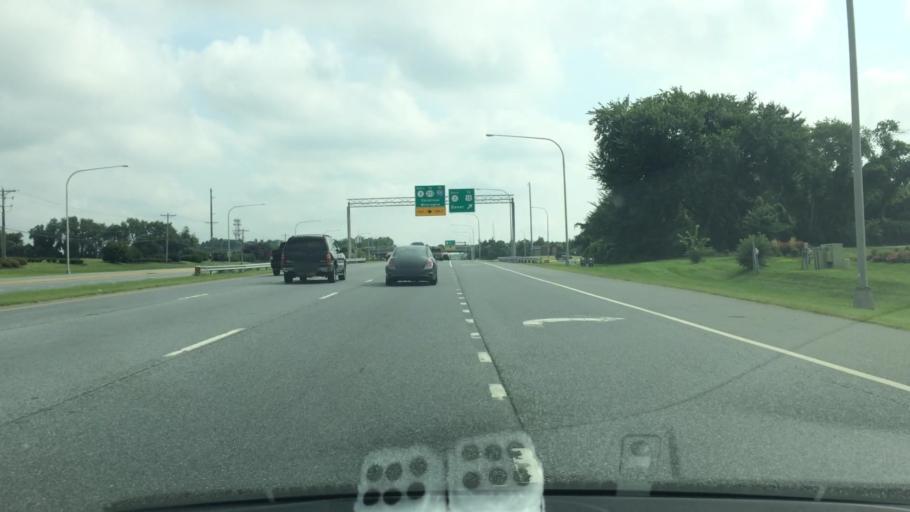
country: US
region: Delaware
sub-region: New Castle County
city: Bear
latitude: 39.6342
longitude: -75.6574
